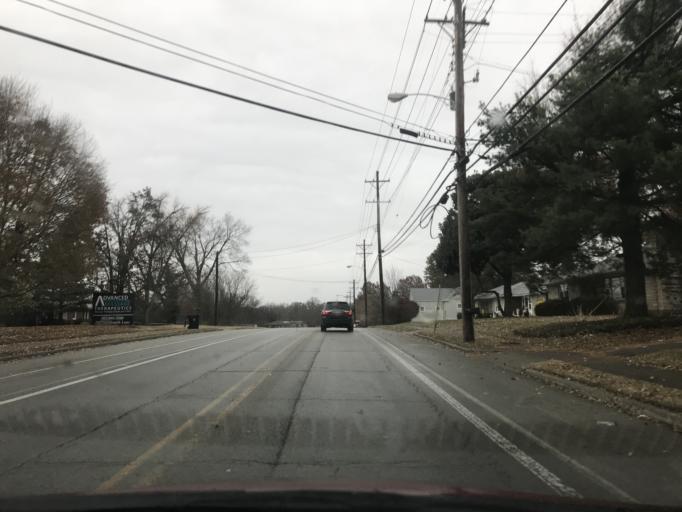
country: US
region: Kentucky
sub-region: Jefferson County
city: West Buechel
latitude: 38.2095
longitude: -85.6672
